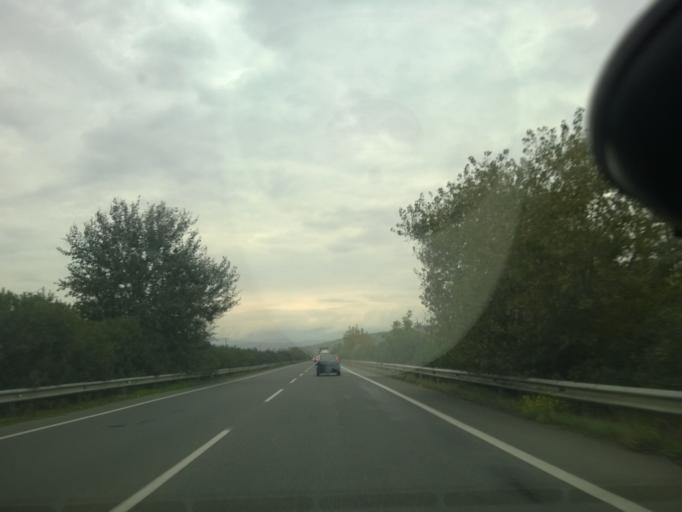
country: GR
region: Central Macedonia
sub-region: Nomos Pellis
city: Mavrovouni
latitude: 40.7913
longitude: 22.1698
